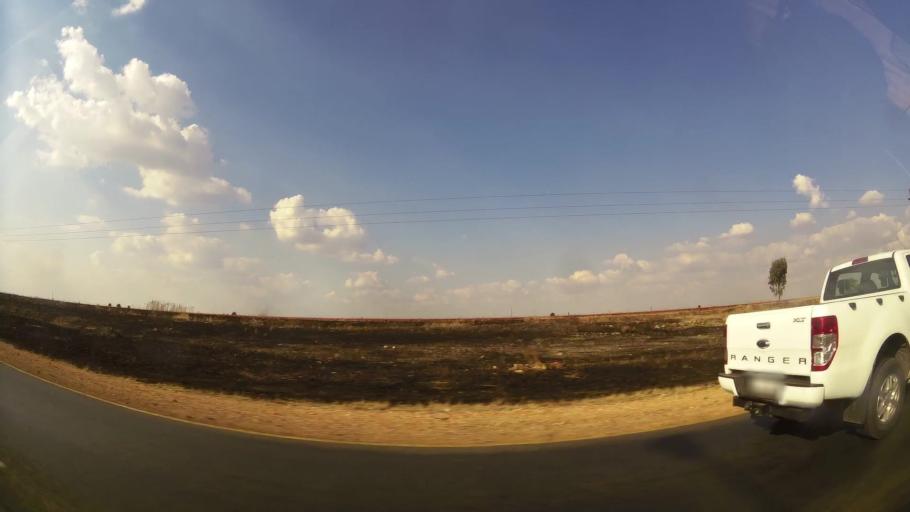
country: ZA
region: Gauteng
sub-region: Ekurhuleni Metropolitan Municipality
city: Springs
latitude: -26.3428
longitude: 28.3416
